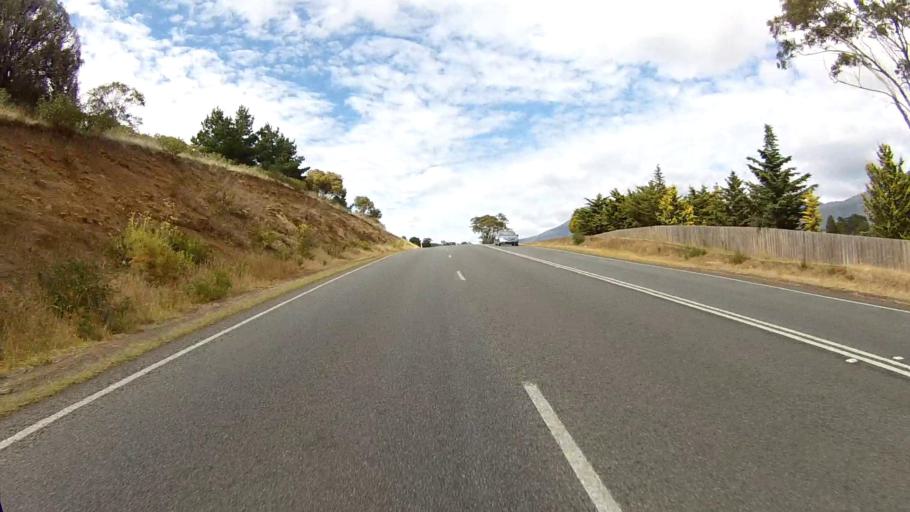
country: AU
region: Tasmania
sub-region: Brighton
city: Old Beach
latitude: -42.7912
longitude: 147.2932
